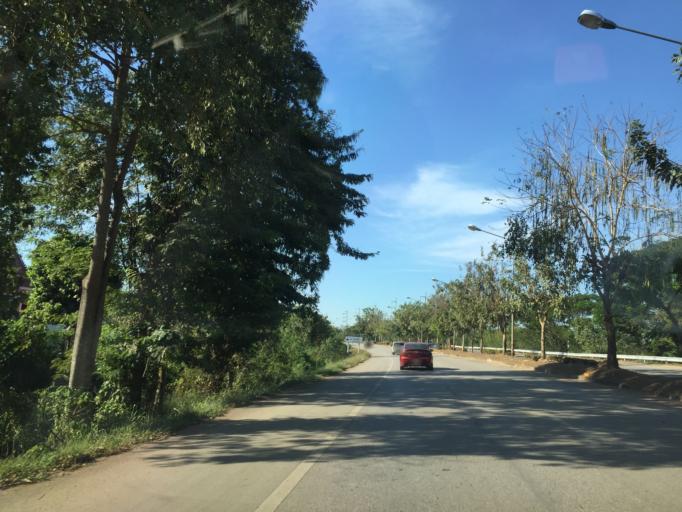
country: TH
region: Loei
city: Wang Saphung
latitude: 17.3149
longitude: 101.7706
